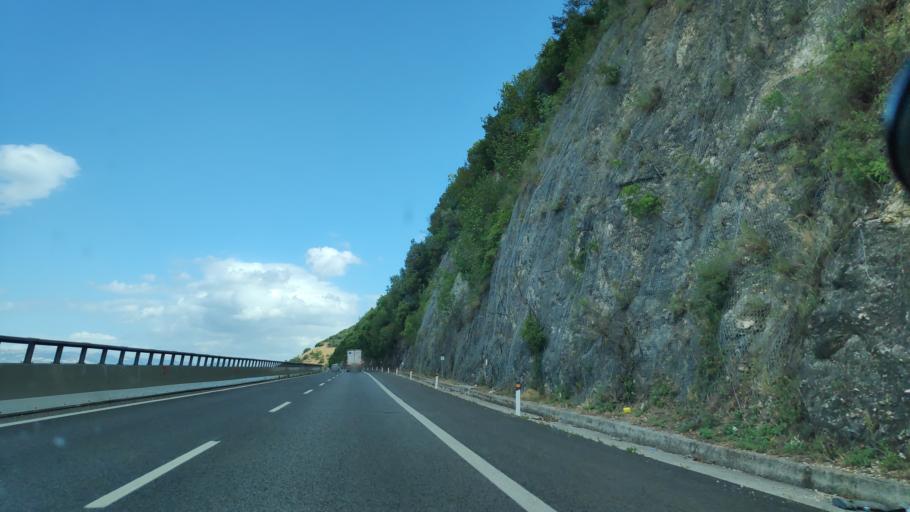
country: IT
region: Campania
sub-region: Provincia di Salerno
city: Sicignano degli Alburni
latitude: 40.5891
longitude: 15.3334
